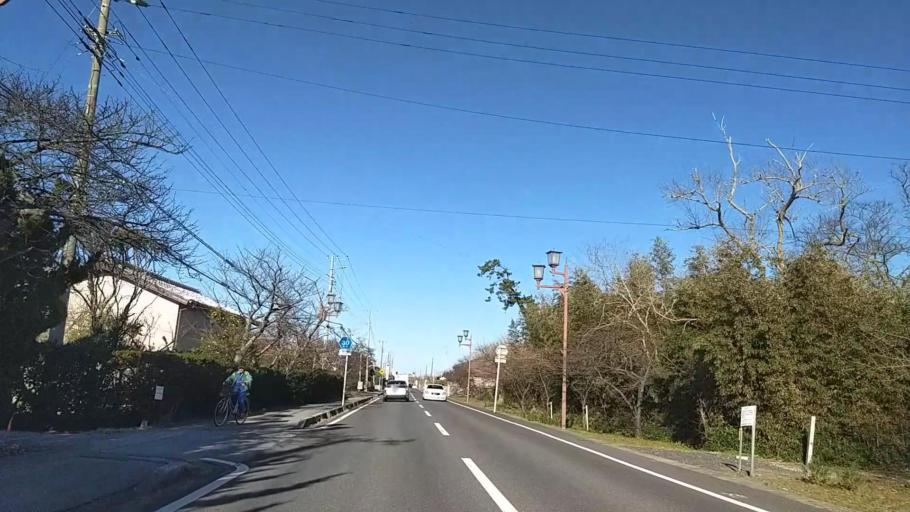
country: JP
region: Chiba
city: Mobara
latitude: 35.4328
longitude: 140.3967
